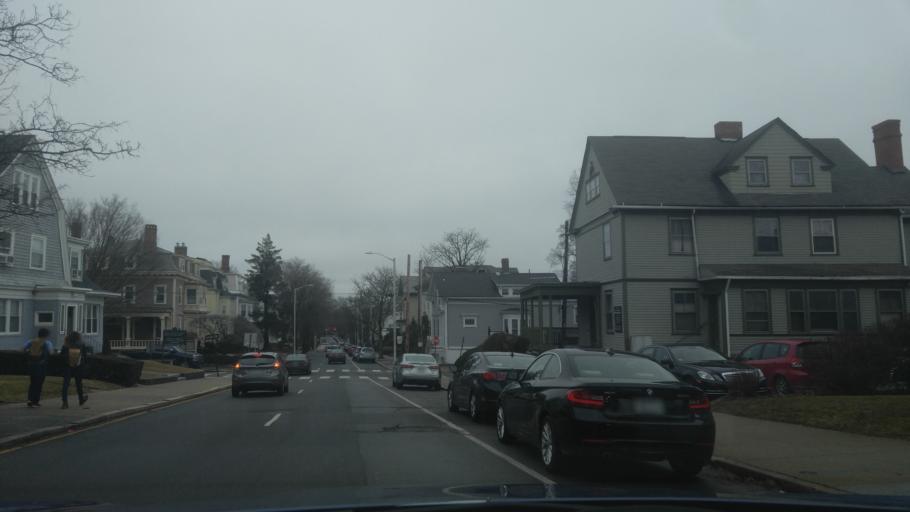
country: US
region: Rhode Island
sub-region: Providence County
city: Providence
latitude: 41.8277
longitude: -71.3936
